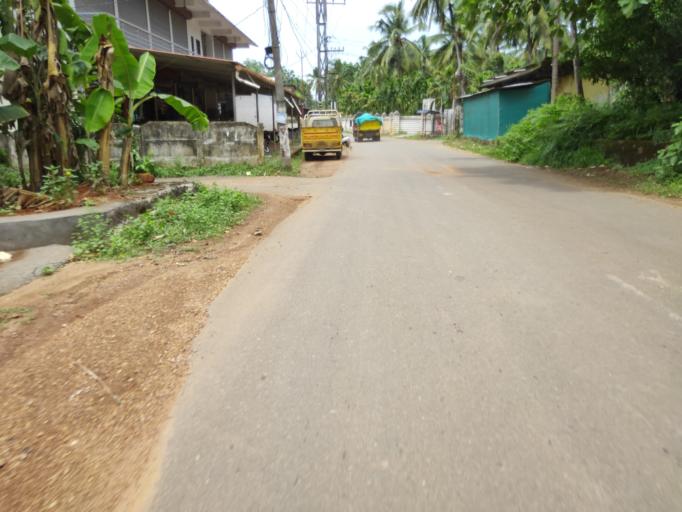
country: IN
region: Kerala
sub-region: Malappuram
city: Manjeri
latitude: 11.2005
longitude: 76.2602
